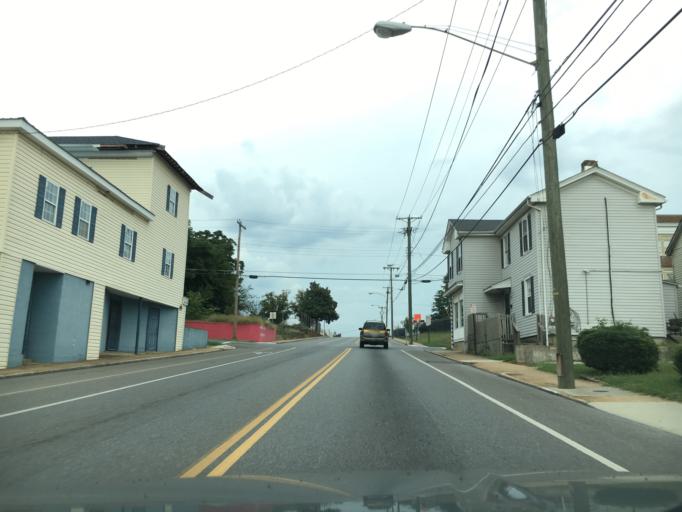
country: US
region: Virginia
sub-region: City of Lynchburg
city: Lynchburg
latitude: 37.4054
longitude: -79.1525
